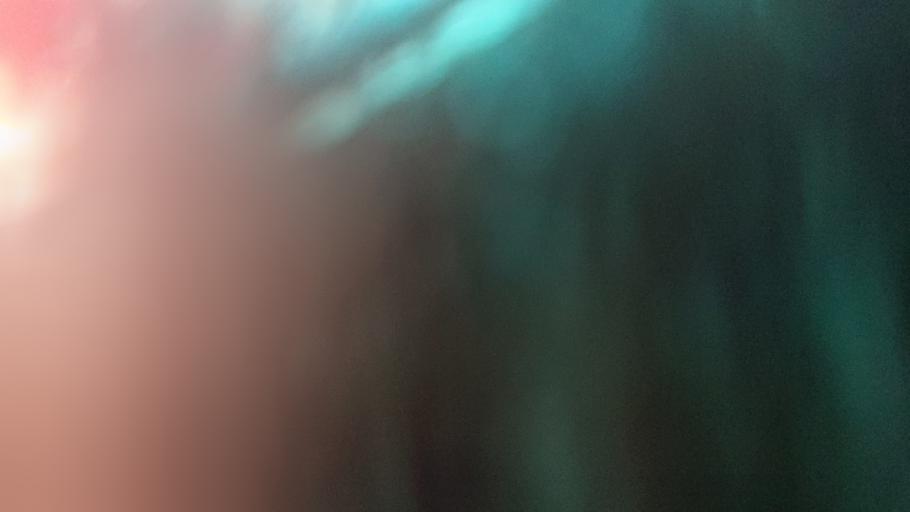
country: TW
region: Taiwan
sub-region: Chiayi
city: Taibao
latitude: 23.7068
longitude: 120.1824
